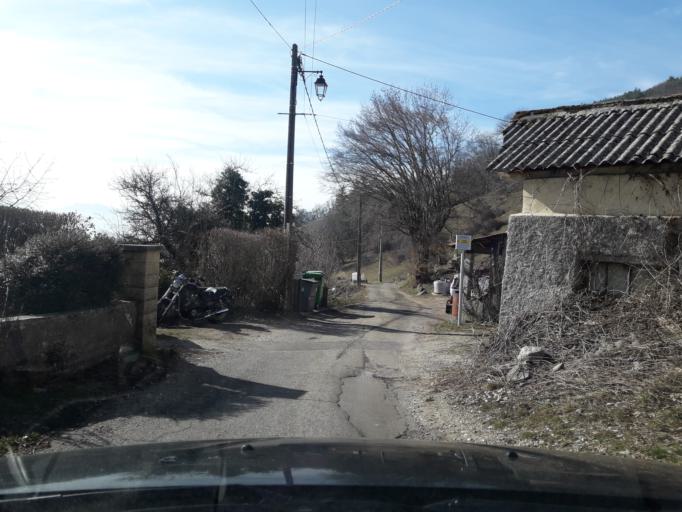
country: FR
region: Rhone-Alpes
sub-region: Departement de l'Isere
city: Corenc
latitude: 45.2271
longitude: 5.7503
